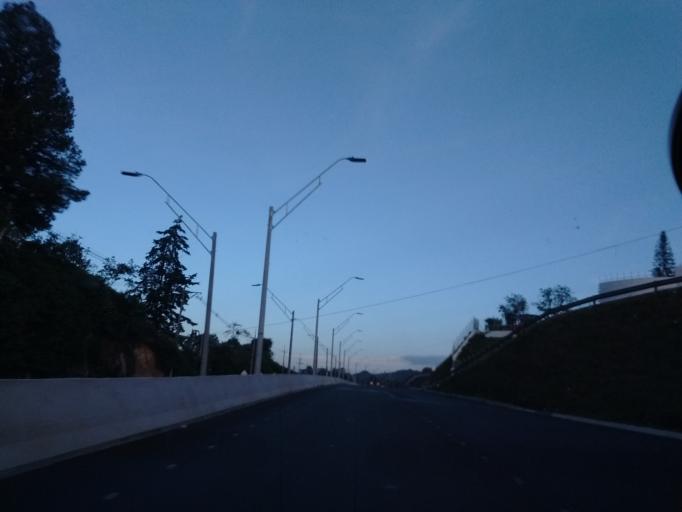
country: CO
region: Antioquia
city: Marinilla
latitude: 6.1483
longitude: -75.3119
